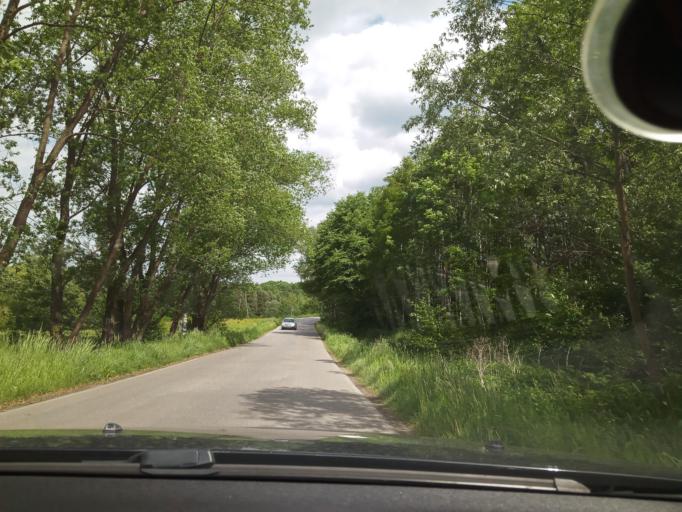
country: PL
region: Lesser Poland Voivodeship
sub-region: Powiat bochenski
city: Lapanow
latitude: 49.8526
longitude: 20.2582
